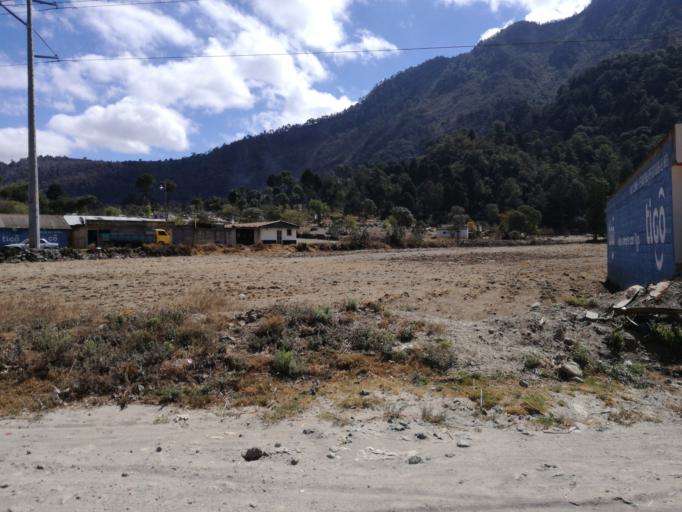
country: GT
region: Quetzaltenango
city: Quetzaltenango
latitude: 14.7994
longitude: -91.5376
